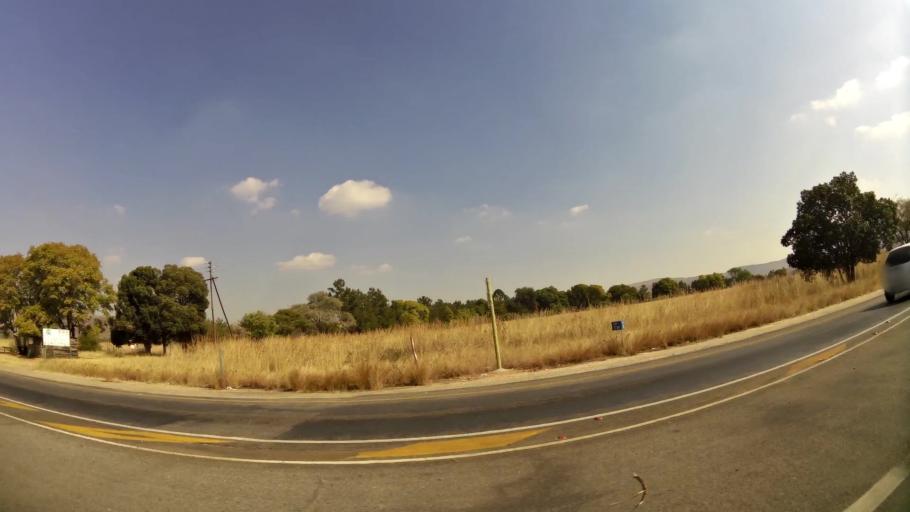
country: ZA
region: North-West
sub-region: Bojanala Platinum District Municipality
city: Rustenburg
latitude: -25.5232
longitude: 27.1083
